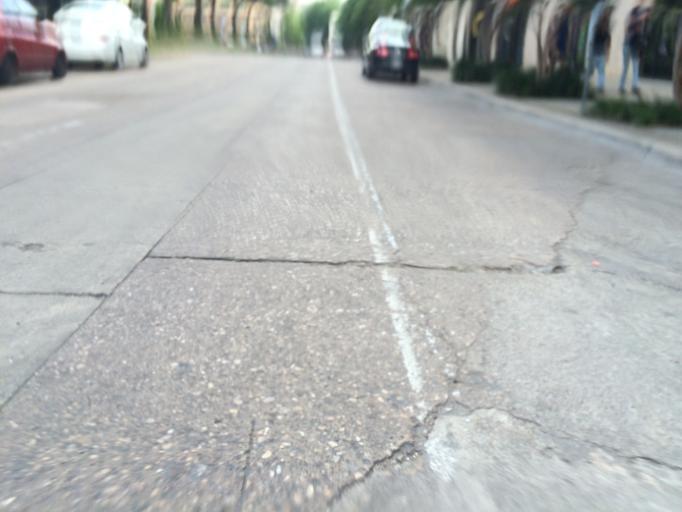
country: US
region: Texas
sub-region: Travis County
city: Austin
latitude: 30.2925
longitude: -97.7427
